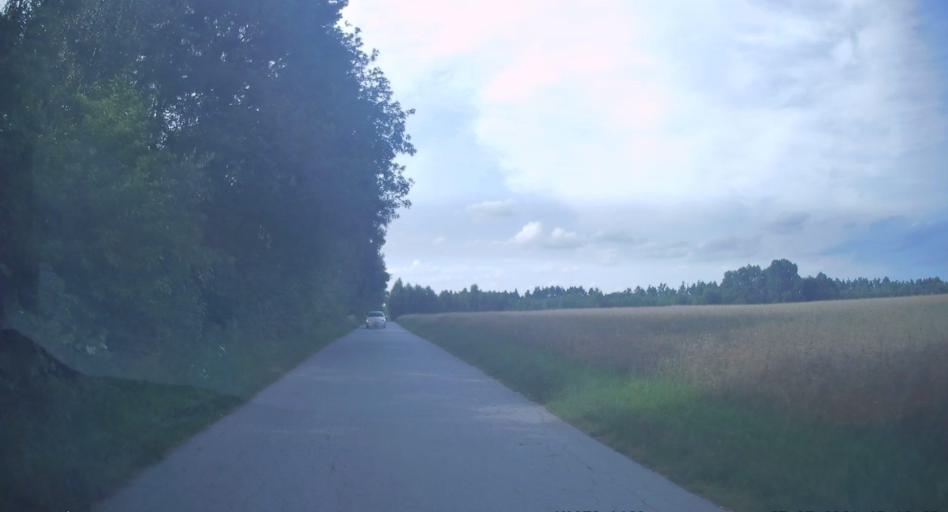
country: PL
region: Lodz Voivodeship
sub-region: Powiat rawski
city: Rawa Mazowiecka
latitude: 51.6962
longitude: 20.2505
